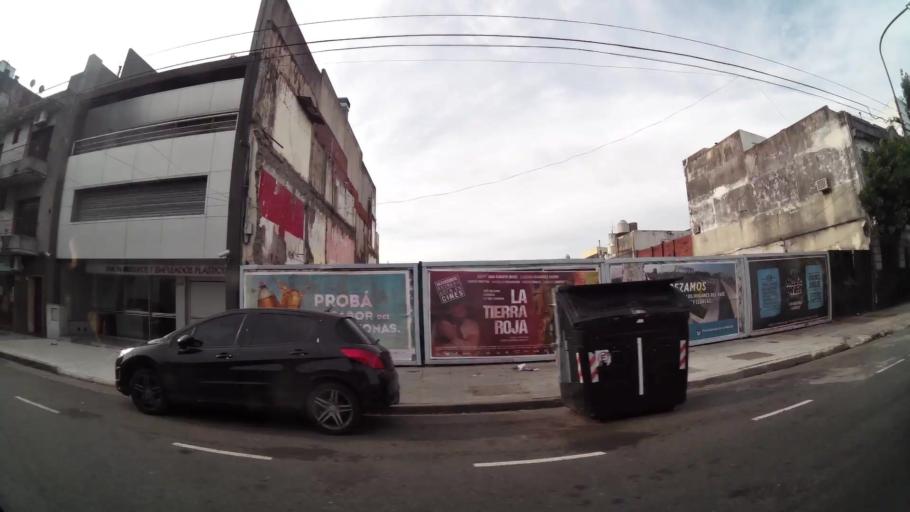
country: AR
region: Buenos Aires F.D.
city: Buenos Aires
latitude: -34.6310
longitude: -58.4223
